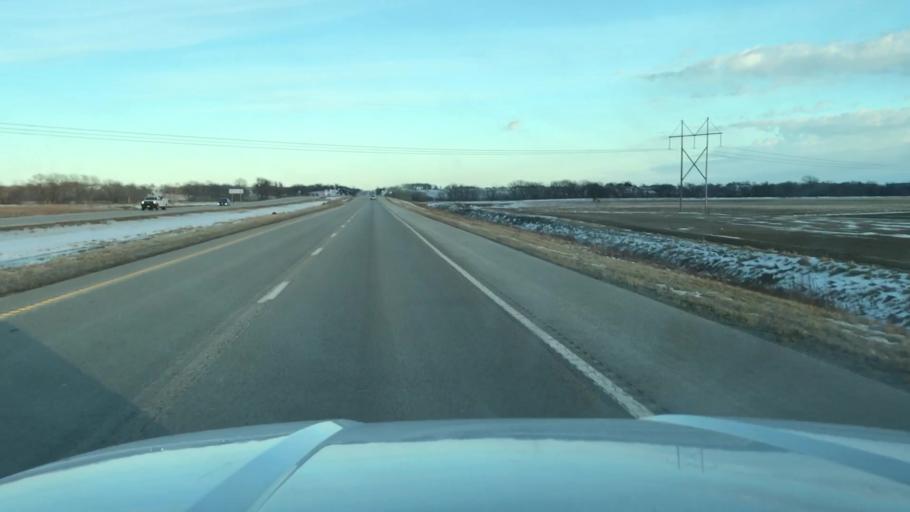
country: US
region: Missouri
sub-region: Buchanan County
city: Saint Joseph
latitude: 39.7474
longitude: -94.7345
